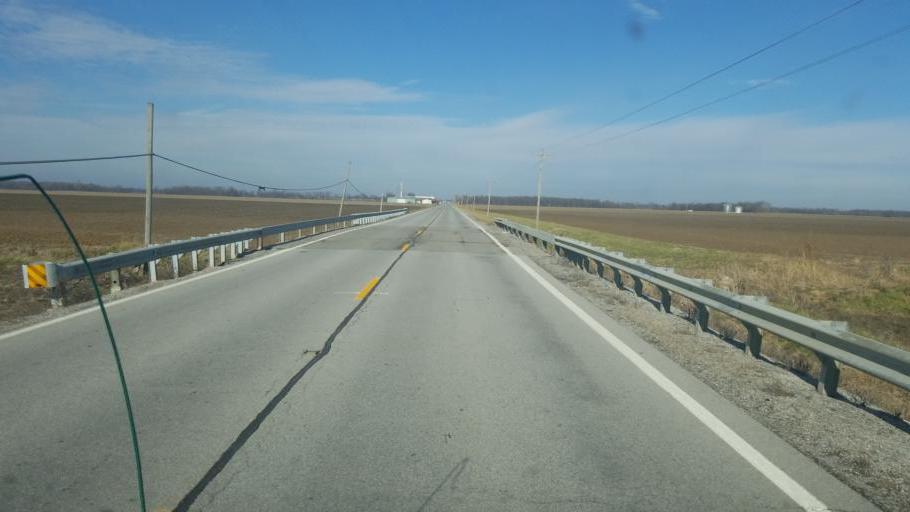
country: US
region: Illinois
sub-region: Saline County
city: Eldorado
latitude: 37.8631
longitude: -88.4529
